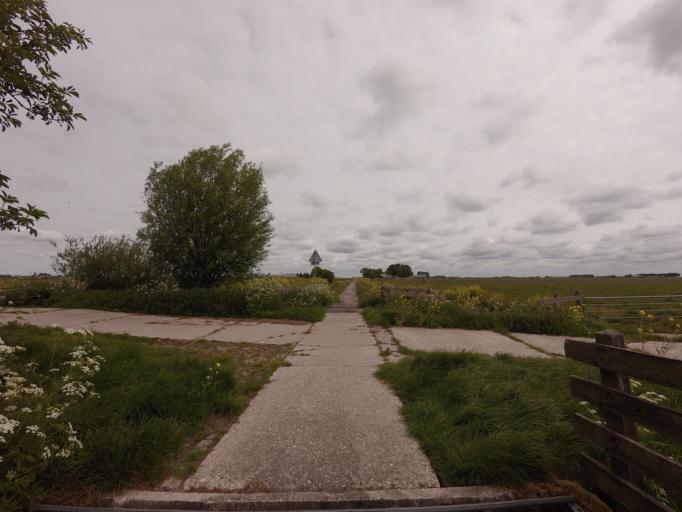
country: NL
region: Friesland
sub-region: Sudwest Fryslan
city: Koudum
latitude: 52.9478
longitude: 5.4665
